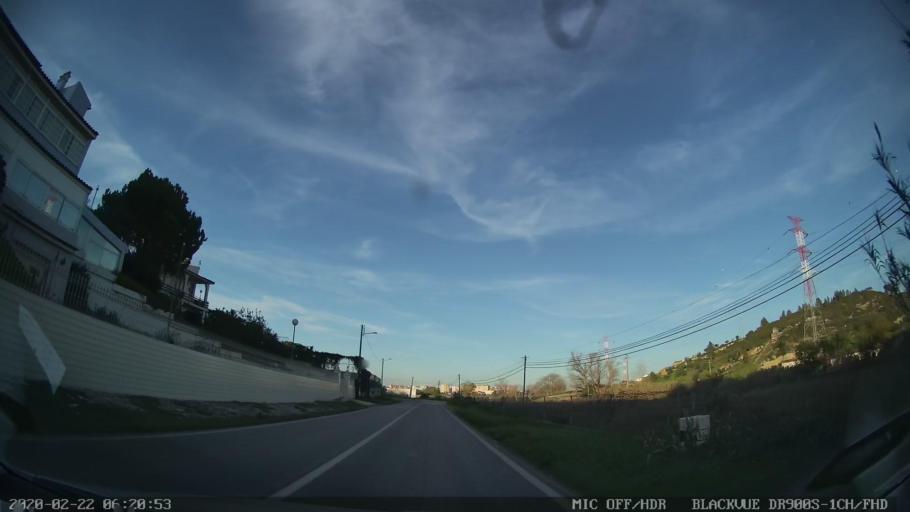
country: PT
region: Lisbon
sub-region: Alenquer
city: Carregado
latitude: 39.0122
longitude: -8.9832
